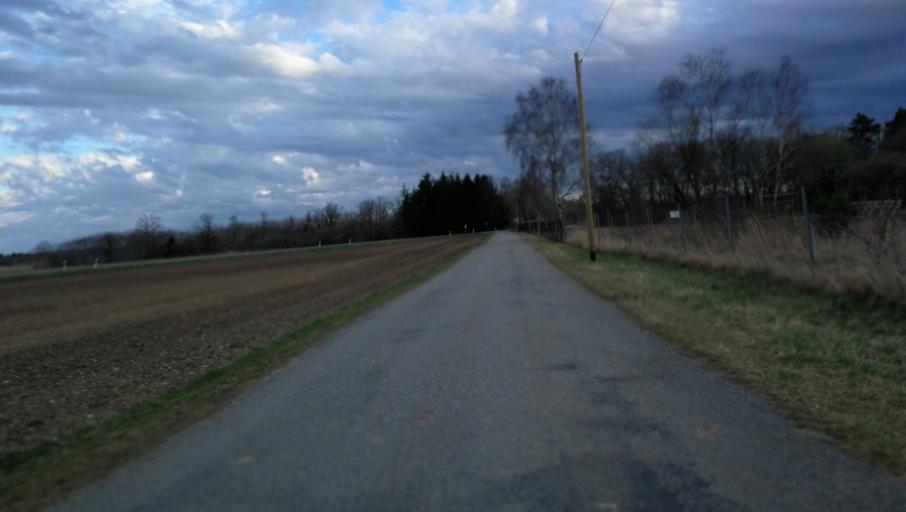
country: DE
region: Bavaria
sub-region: Upper Bavaria
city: Fuerstenfeldbruck
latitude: 48.1960
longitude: 11.2354
